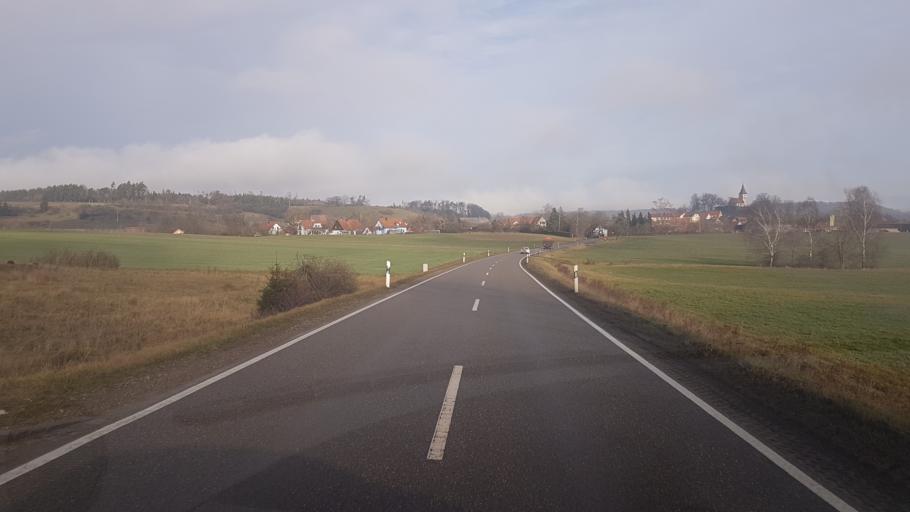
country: DE
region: Bavaria
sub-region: Regierungsbezirk Mittelfranken
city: Dombuhl
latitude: 49.2506
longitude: 10.2778
